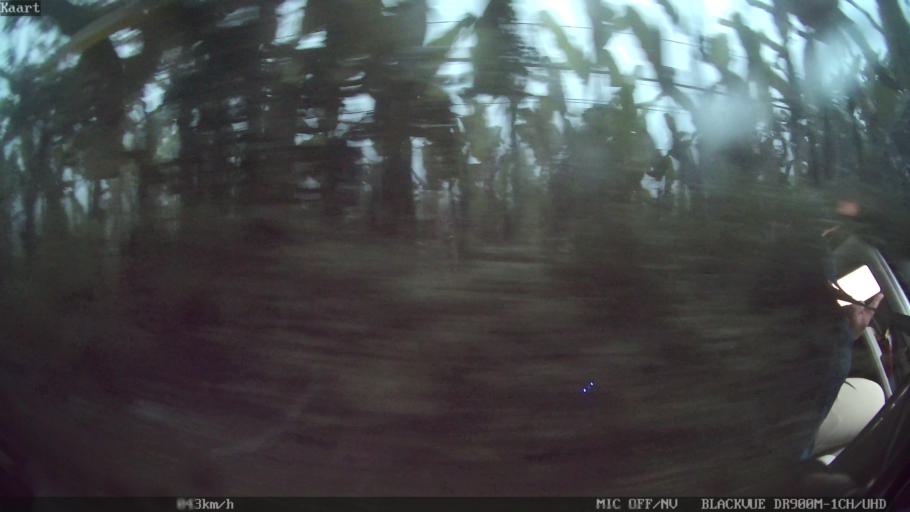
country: ID
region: Bali
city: Banjar Taro Kelod
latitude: -8.3446
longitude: 115.2799
